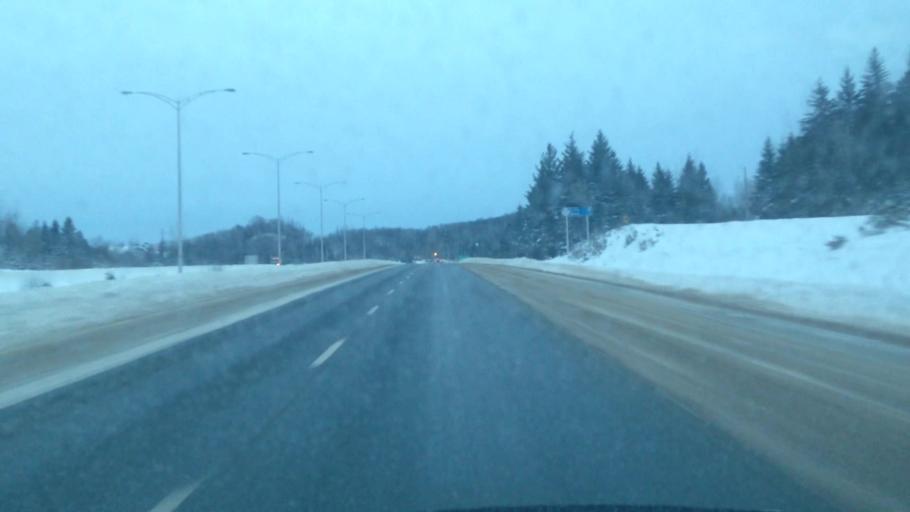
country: CA
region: Quebec
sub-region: Laurentides
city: Mont-Tremblant
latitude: 46.1123
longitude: -74.4749
